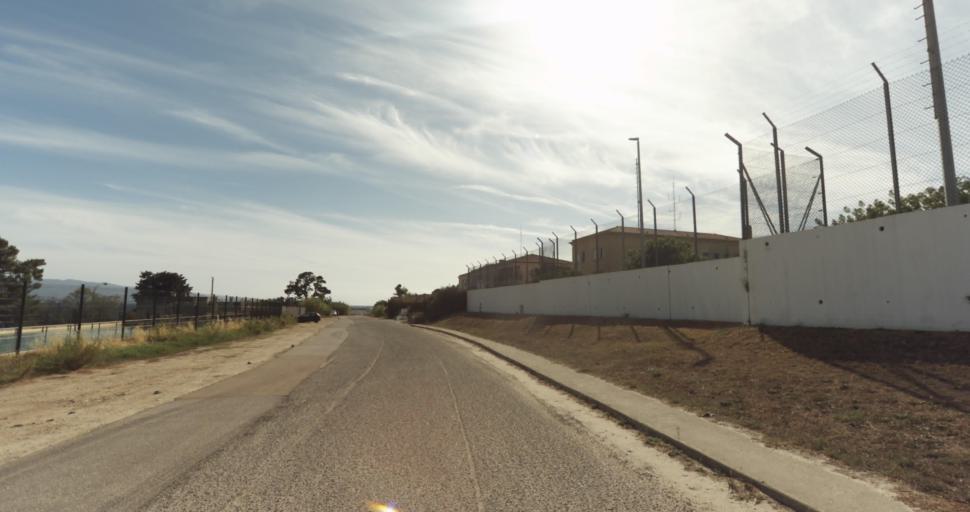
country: FR
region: Corsica
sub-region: Departement de la Corse-du-Sud
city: Ajaccio
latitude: 41.9275
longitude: 8.7673
